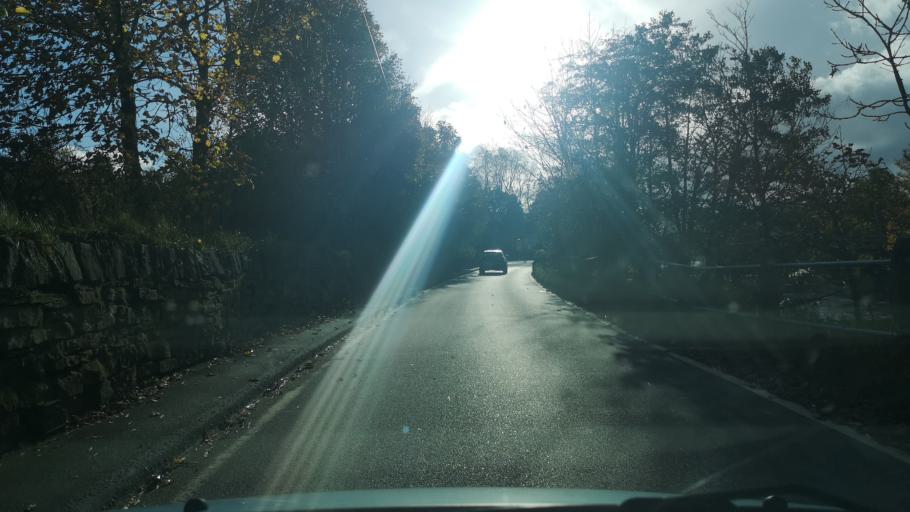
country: GB
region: England
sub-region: Kirklees
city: Mirfield
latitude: 53.6717
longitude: -1.6754
